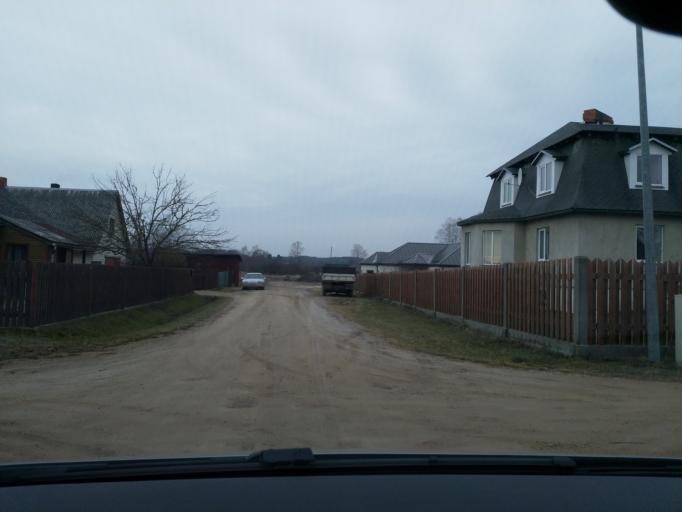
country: LV
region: Kuldigas Rajons
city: Kuldiga
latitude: 56.9570
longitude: 21.9710
